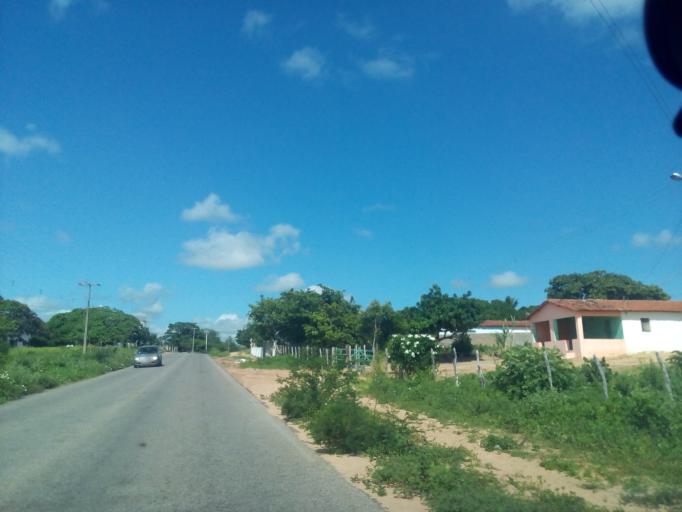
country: BR
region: Rio Grande do Norte
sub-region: Sao Paulo Do Potengi
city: Sao Paulo do Potengi
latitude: -5.9149
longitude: -35.7095
